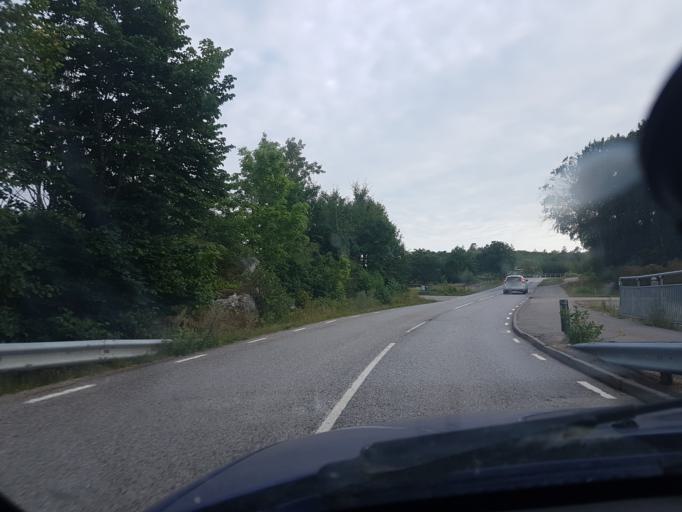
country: SE
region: Vaestra Goetaland
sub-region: Lysekils Kommun
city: Lysekil
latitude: 58.2425
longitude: 11.4686
